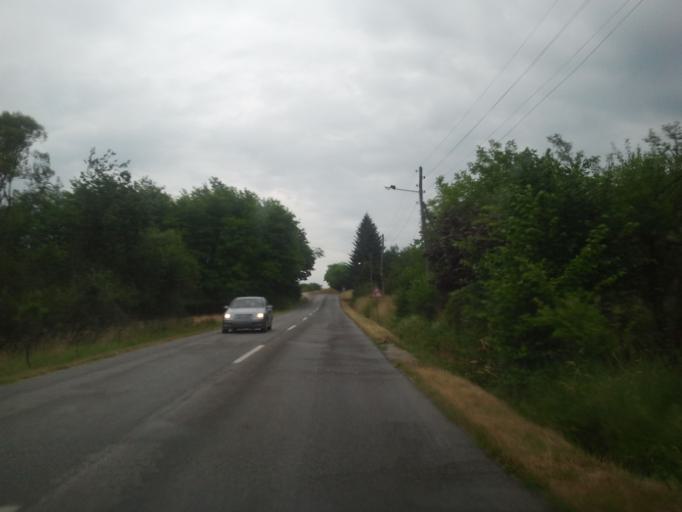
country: HR
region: Sisacko-Moslavacka
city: Gvozd
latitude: 45.3461
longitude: 15.8839
